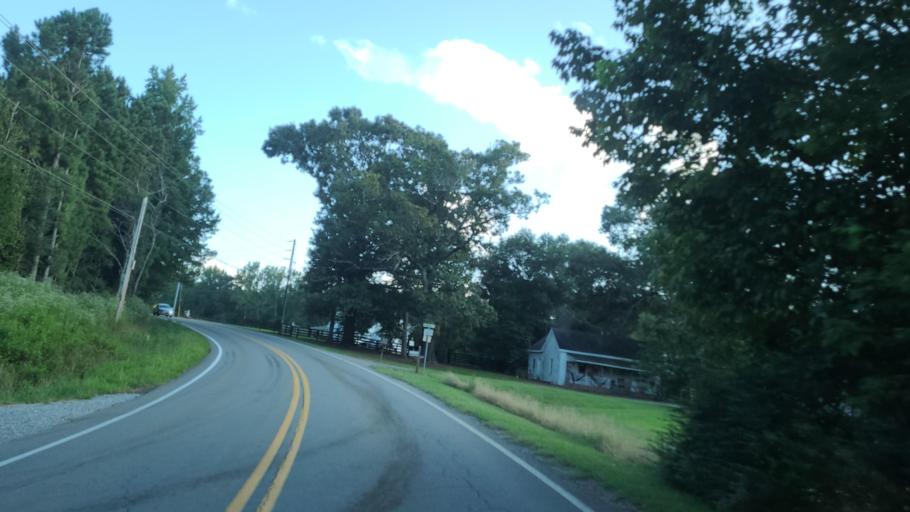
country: US
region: Georgia
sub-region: Fulton County
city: Milton
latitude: 34.1575
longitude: -84.3844
